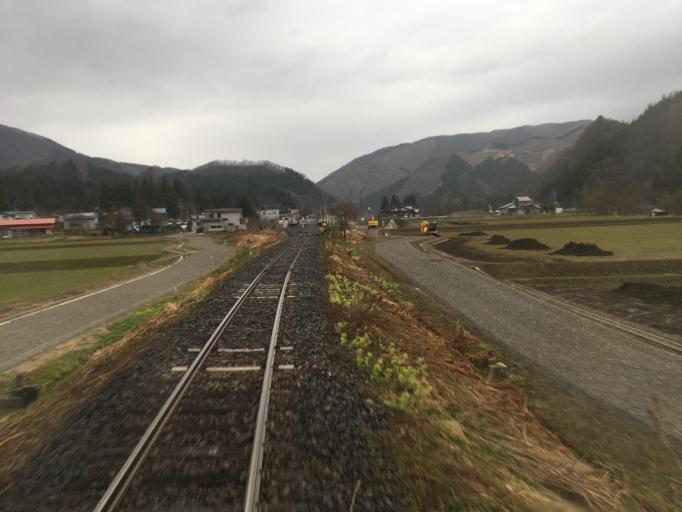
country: JP
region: Akita
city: Kakunodatemachi
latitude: 39.6862
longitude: 140.5526
